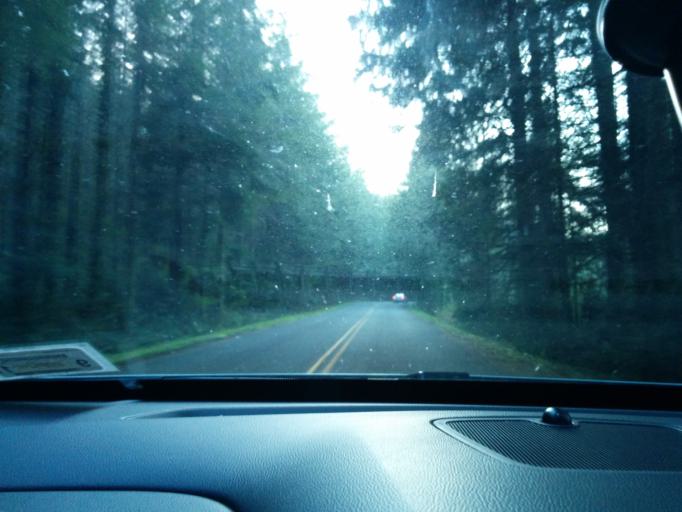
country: US
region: Washington
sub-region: Snohomish County
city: Sultan
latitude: 47.8980
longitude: -121.7582
